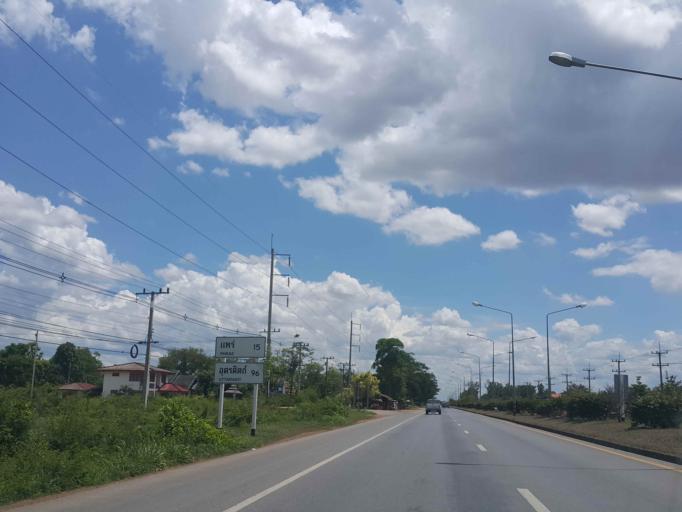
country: TH
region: Phrae
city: Nong Muang Khai
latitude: 18.2483
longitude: 100.2255
